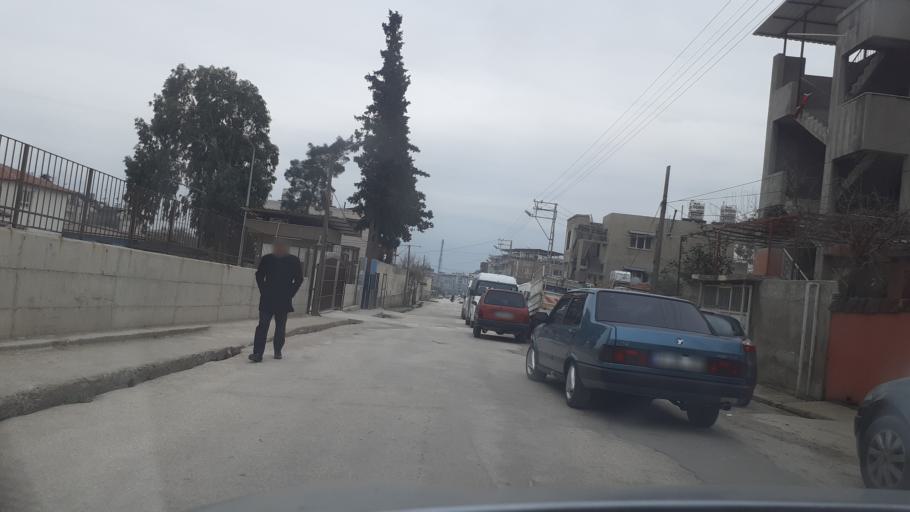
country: TR
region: Hatay
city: Kirikhan
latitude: 36.4876
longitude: 36.3557
